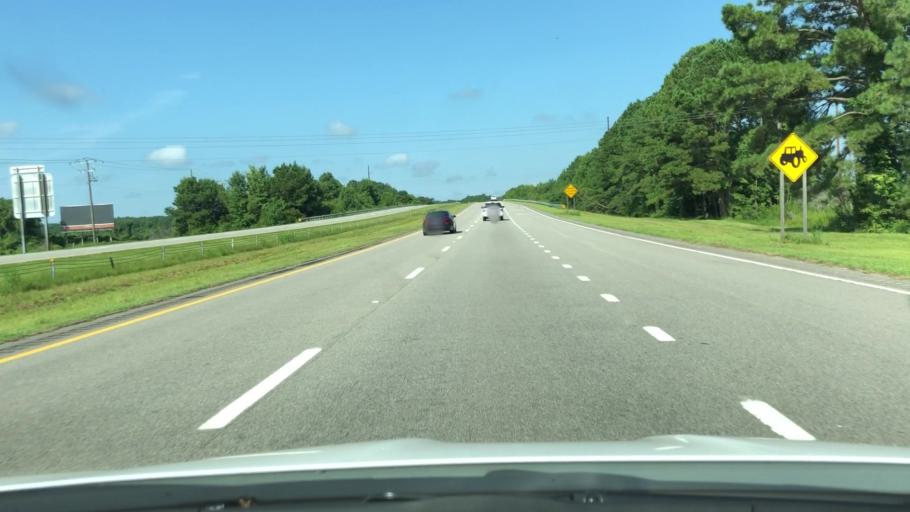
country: US
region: North Carolina
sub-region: Chowan County
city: Edenton
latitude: 36.0906
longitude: -76.5781
